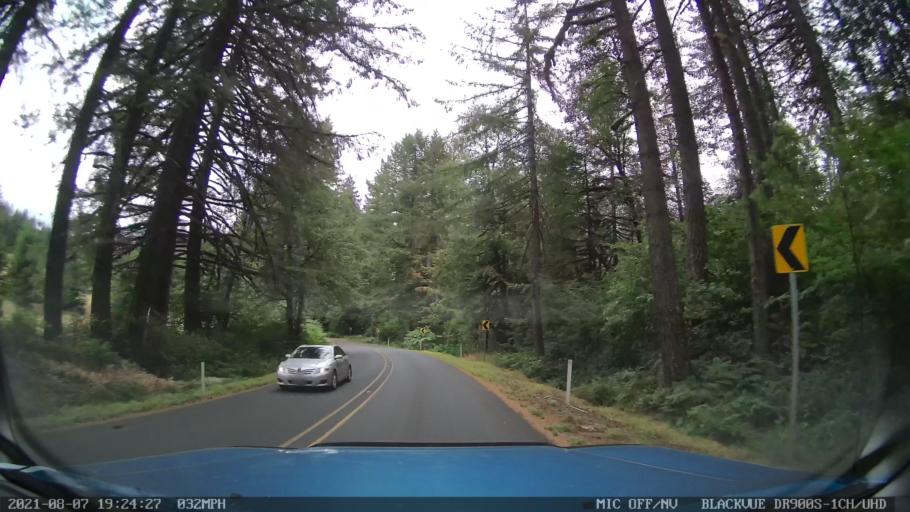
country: US
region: Oregon
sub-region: Linn County
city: Lyons
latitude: 44.8533
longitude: -122.6578
